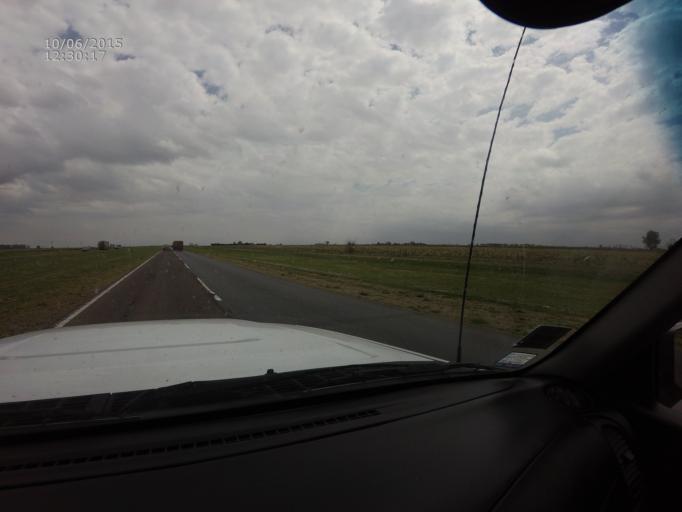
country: AR
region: Santa Fe
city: Carcarana
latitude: -32.8890
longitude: -61.0990
